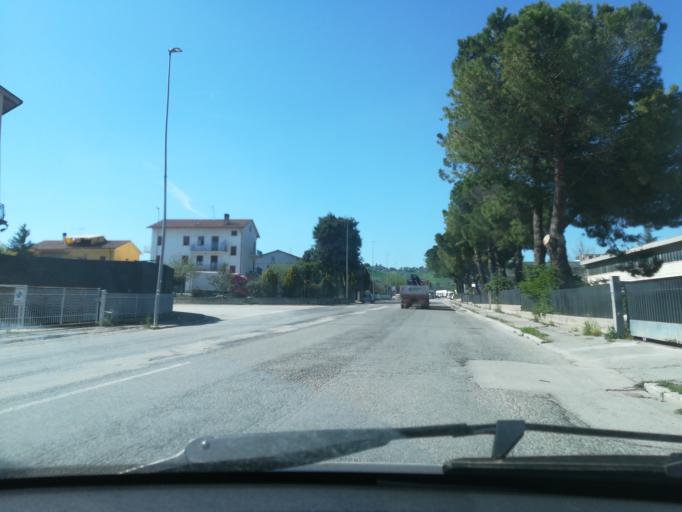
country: IT
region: The Marches
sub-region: Provincia di Macerata
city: Piediripa
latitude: 43.2767
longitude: 13.4924
